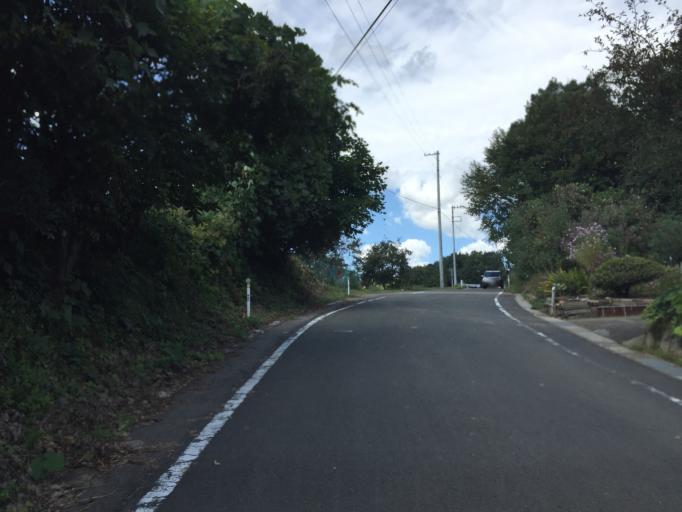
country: JP
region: Fukushima
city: Hobaramachi
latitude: 37.7724
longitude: 140.5186
